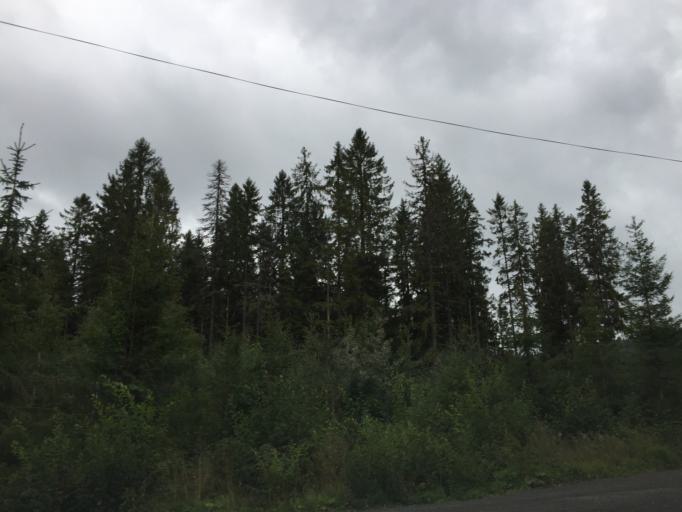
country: NO
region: Akershus
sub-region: Baerum
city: Lysaker
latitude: 60.0196
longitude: 10.5635
